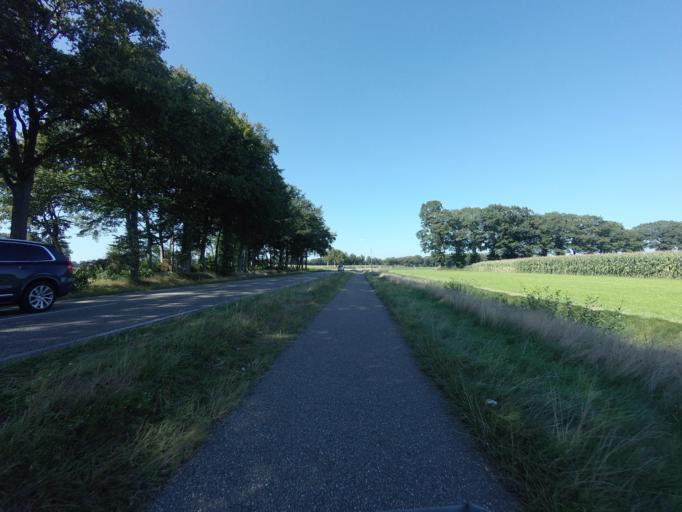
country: NL
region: Overijssel
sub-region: Gemeente Hardenberg
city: Hardenberg
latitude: 52.5326
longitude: 6.5930
